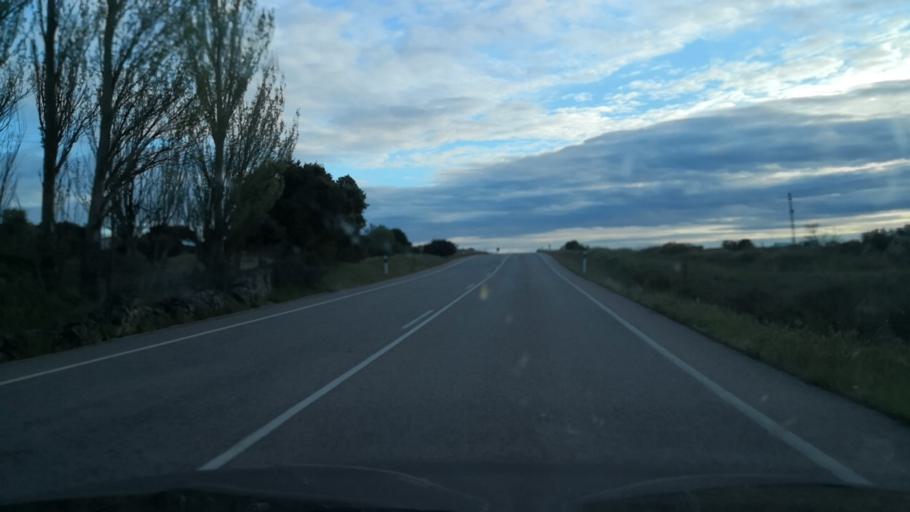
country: ES
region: Extremadura
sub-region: Provincia de Caceres
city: Malpartida de Caceres
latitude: 39.3796
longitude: -6.4471
